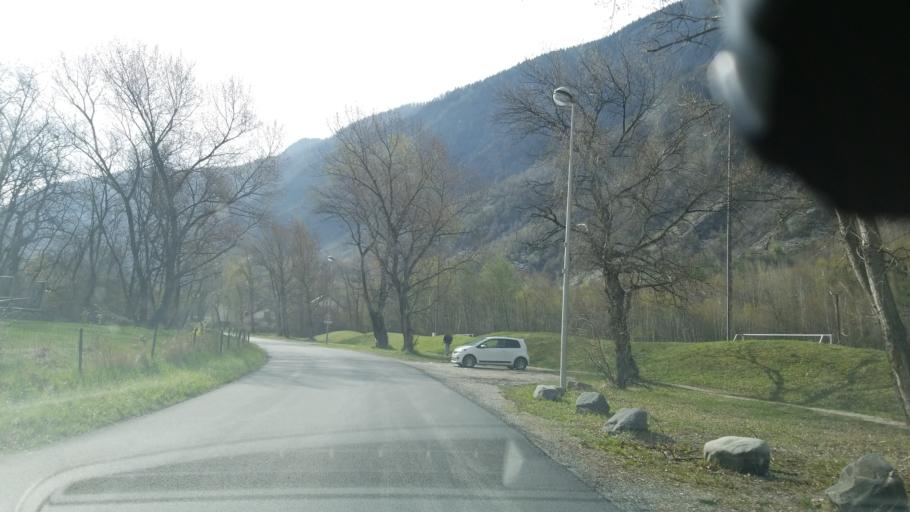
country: FR
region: Rhone-Alpes
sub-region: Departement de la Savoie
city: Villargondran
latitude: 45.2547
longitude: 6.3848
